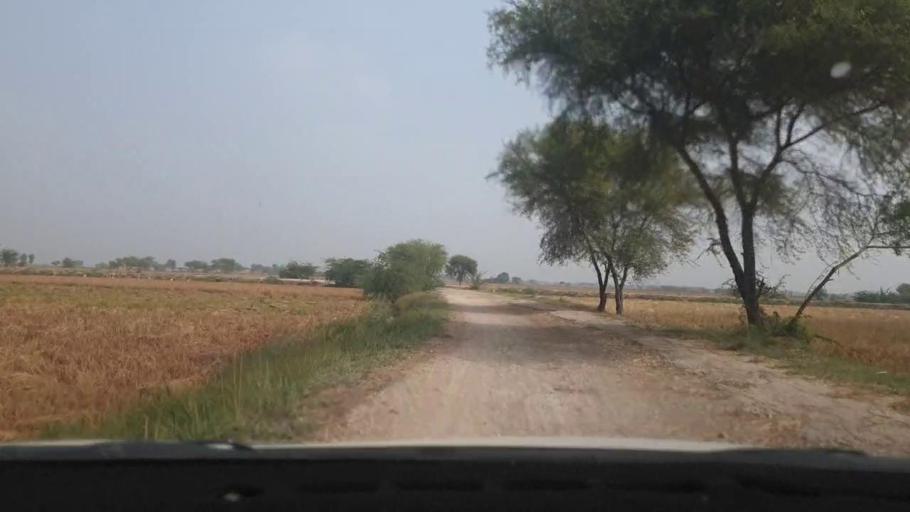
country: PK
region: Sindh
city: Tando Muhammad Khan
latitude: 25.0602
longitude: 68.5428
